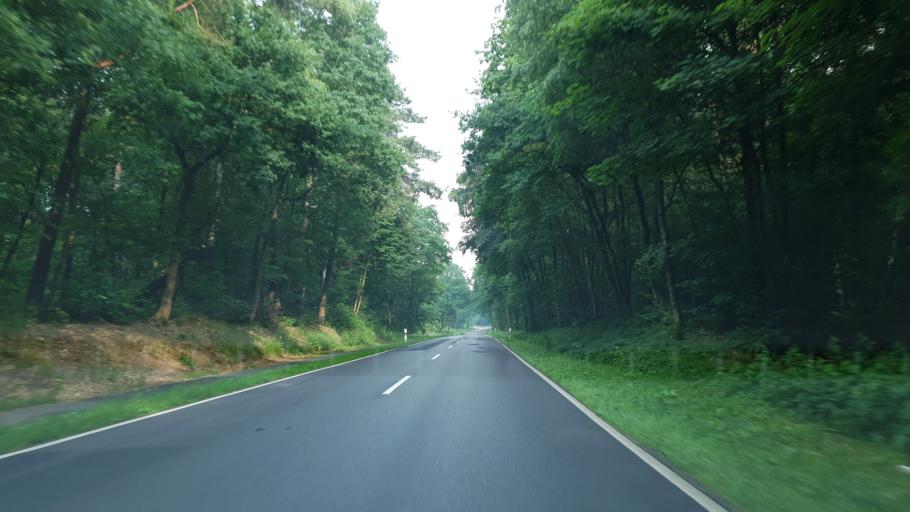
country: DE
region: Lower Saxony
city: Meppen
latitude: 52.6824
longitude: 7.3199
